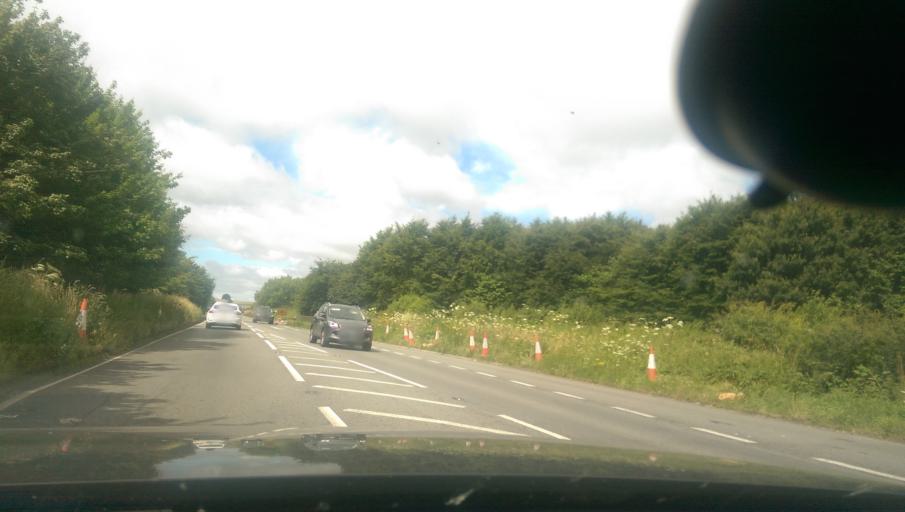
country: GB
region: England
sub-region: Wiltshire
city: Chicklade
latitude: 51.1052
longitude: -2.1645
